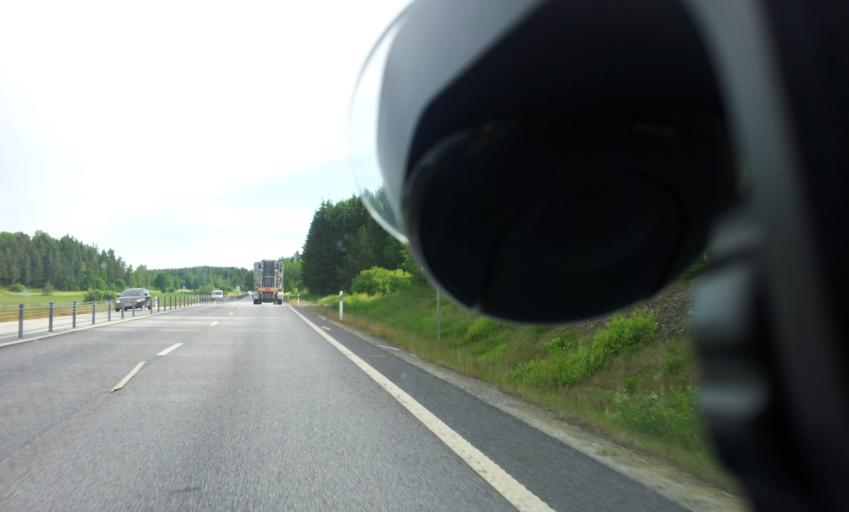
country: SE
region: OEstergoetland
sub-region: Valdemarsviks Kommun
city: Valdemarsvik
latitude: 58.2055
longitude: 16.5569
